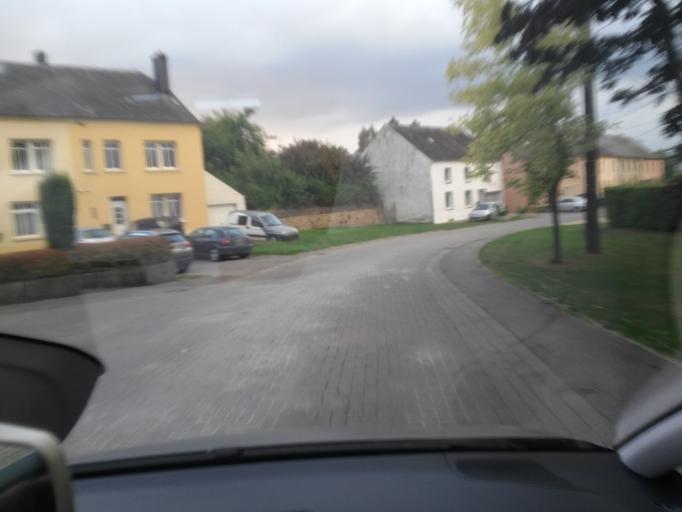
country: BE
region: Wallonia
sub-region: Province du Luxembourg
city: Saint-Leger
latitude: 49.6857
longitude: 5.7102
